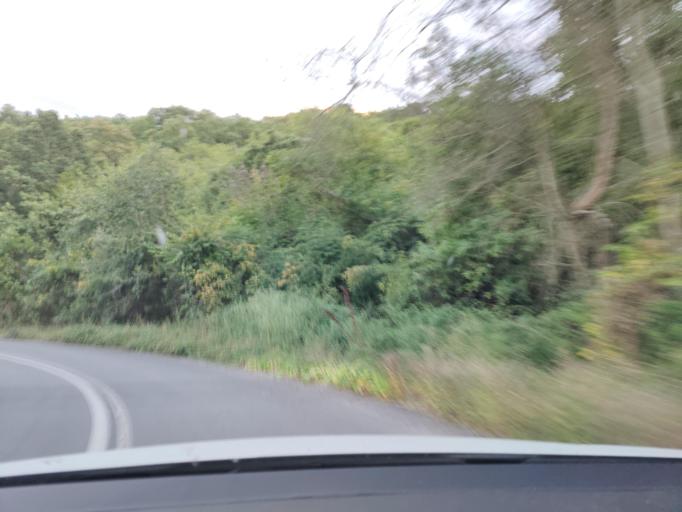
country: GR
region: Central Macedonia
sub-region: Nomos Serron
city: Chrysochorafa
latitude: 41.1769
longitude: 23.1665
